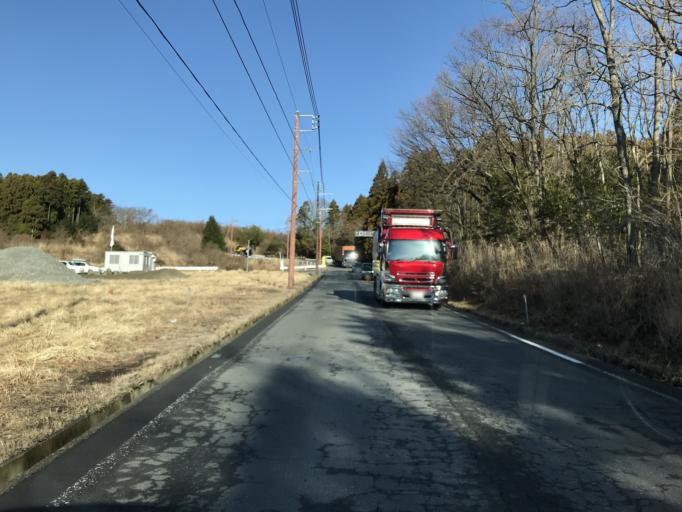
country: JP
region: Shizuoka
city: Gotemba
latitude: 35.2632
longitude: 138.8536
